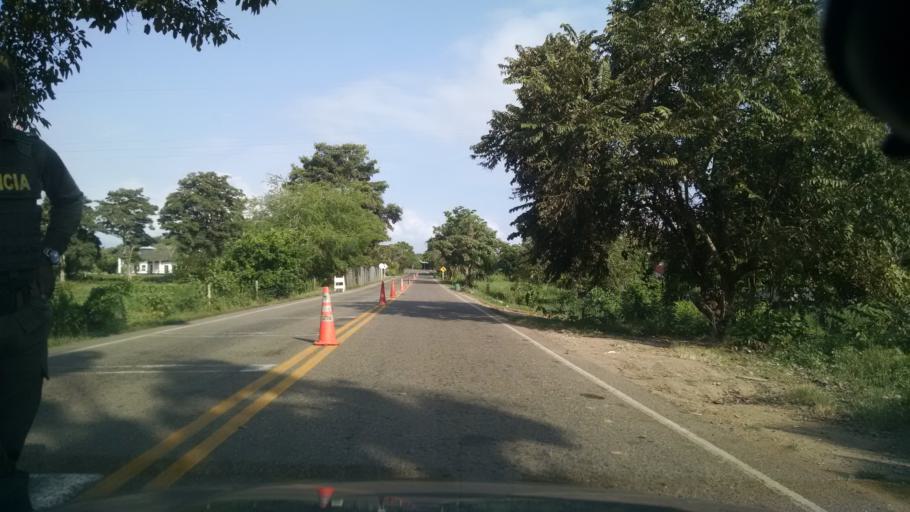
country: CO
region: Antioquia
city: Necocli
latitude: 8.4130
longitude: -76.7556
